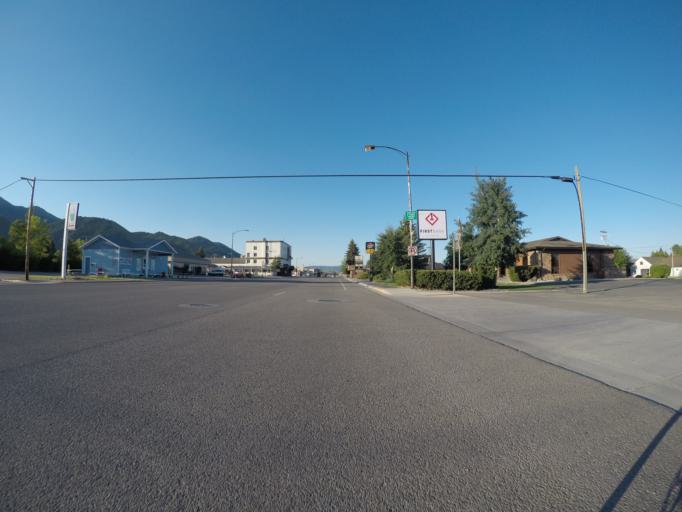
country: US
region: Wyoming
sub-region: Lincoln County
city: Afton
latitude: 42.7274
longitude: -110.9335
